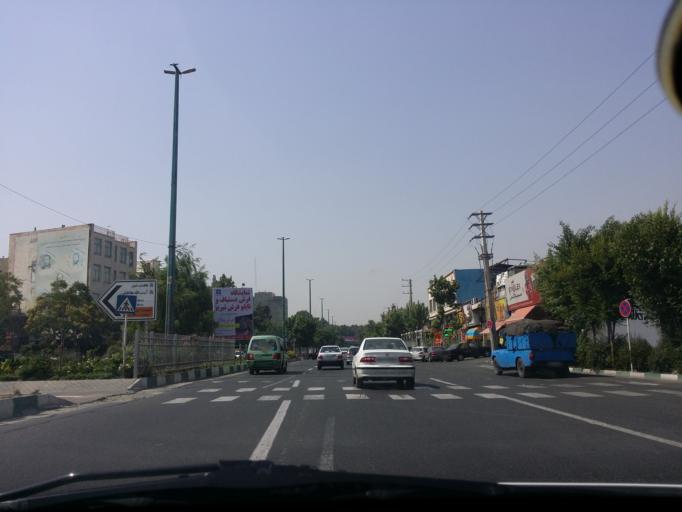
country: IR
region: Alborz
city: Karaj
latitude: 35.7982
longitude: 51.0016
